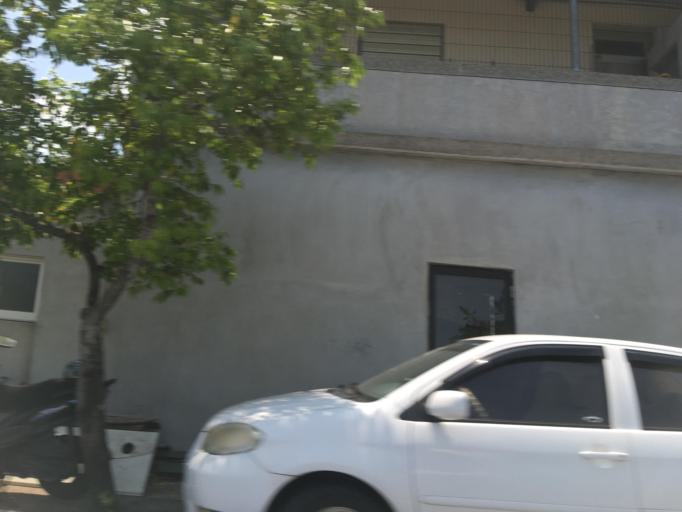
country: TW
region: Taiwan
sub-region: Yilan
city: Yilan
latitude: 24.6614
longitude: 121.7609
